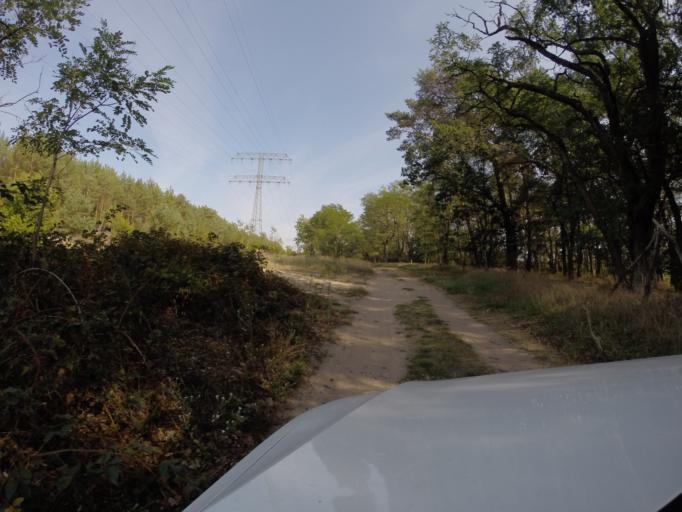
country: DE
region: Brandenburg
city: Baruth
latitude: 52.1252
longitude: 13.5135
